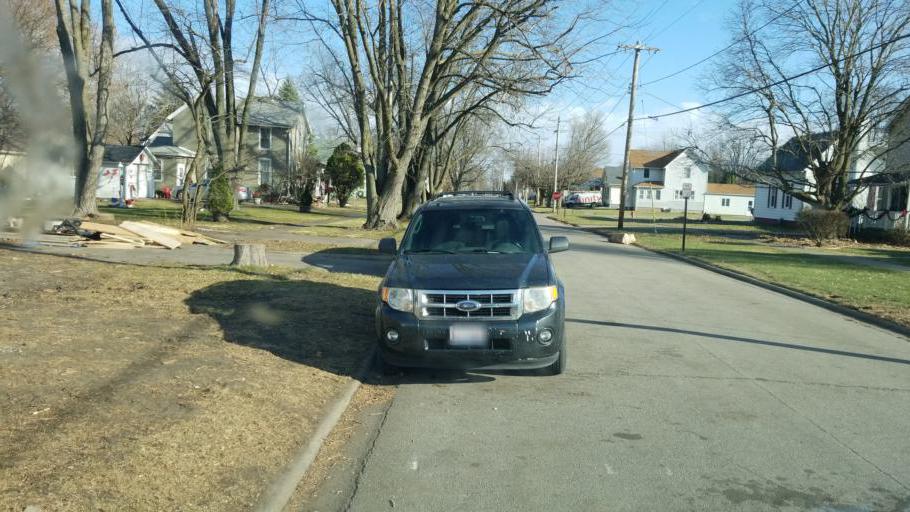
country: US
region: Illinois
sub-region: Warren County
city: Monmouth
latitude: 40.9143
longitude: -90.6577
